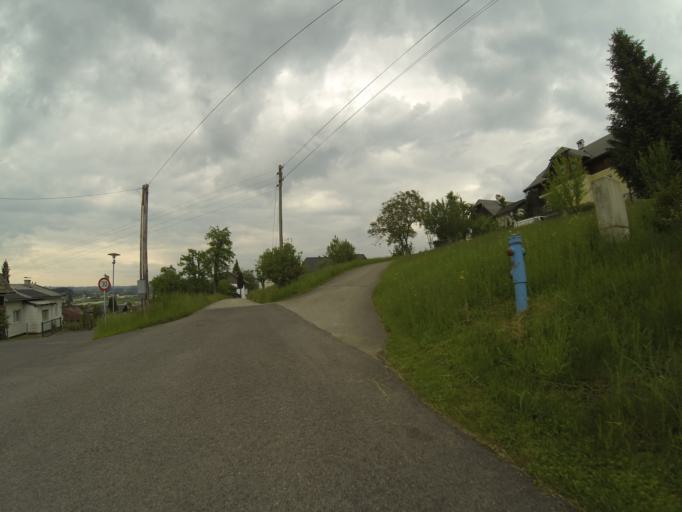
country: AT
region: Upper Austria
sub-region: Politischer Bezirk Gmunden
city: Altmunster
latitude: 47.9284
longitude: 13.7666
